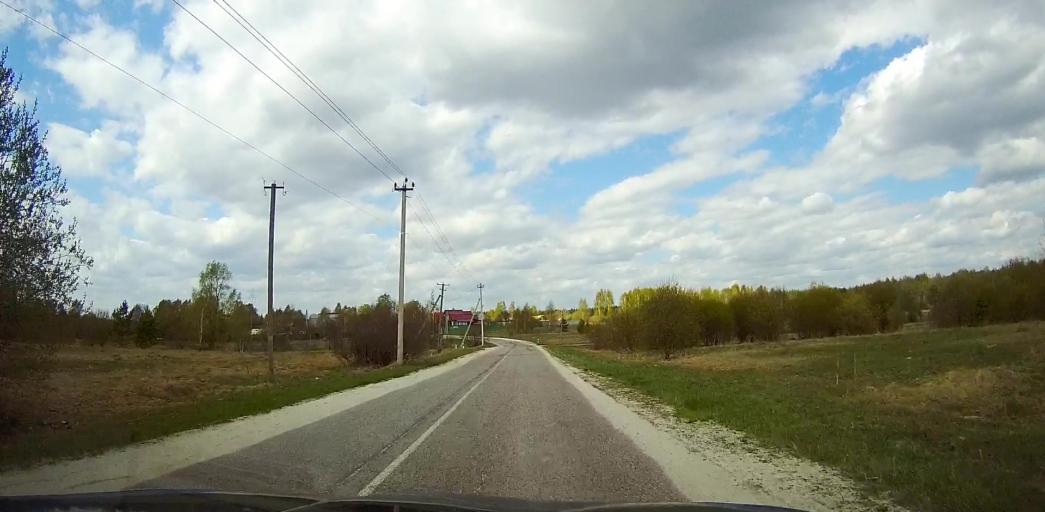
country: RU
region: Moskovskaya
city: Davydovo
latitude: 55.6345
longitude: 38.7828
